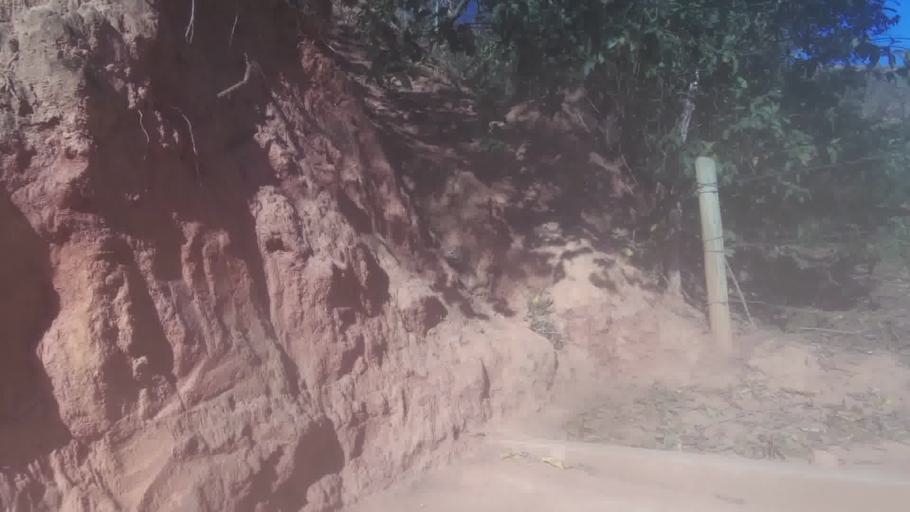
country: BR
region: Espirito Santo
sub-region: Cachoeiro De Itapemirim
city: Cachoeiro de Itapemirim
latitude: -21.0337
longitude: -41.0720
